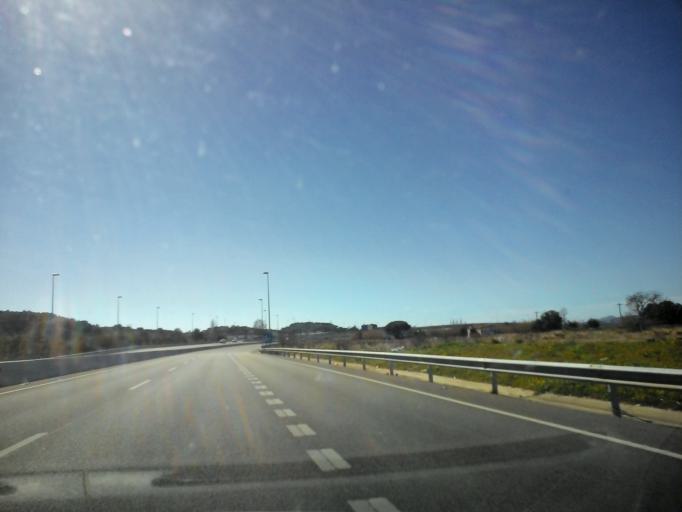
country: ES
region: Catalonia
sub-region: Provincia de Girona
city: Palamos
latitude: 41.8691
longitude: 3.1377
